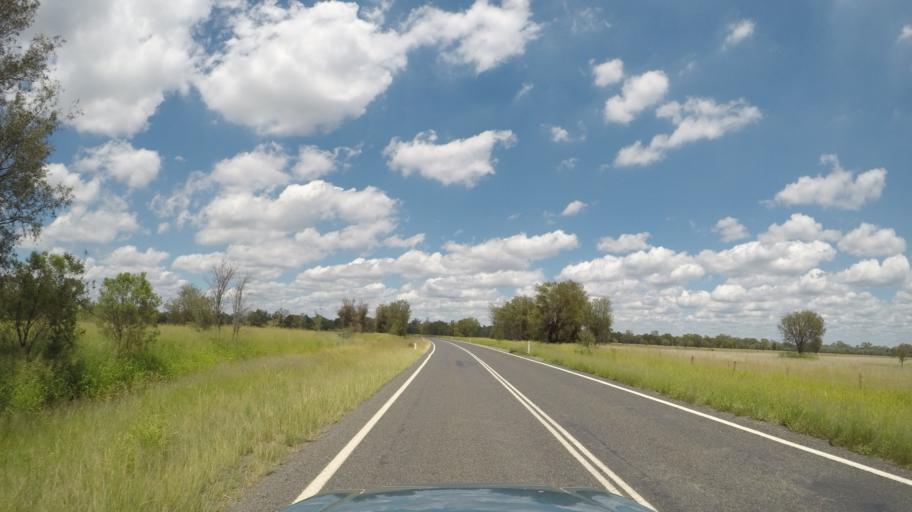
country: AU
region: Queensland
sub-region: Western Downs
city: Dalby
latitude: -27.9545
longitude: 151.1303
